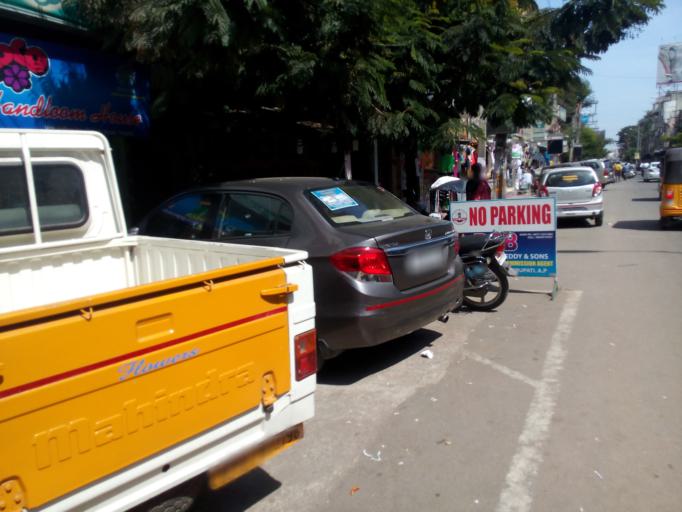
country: IN
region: Andhra Pradesh
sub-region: Chittoor
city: Tirupati
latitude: 13.6312
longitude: 79.4161
